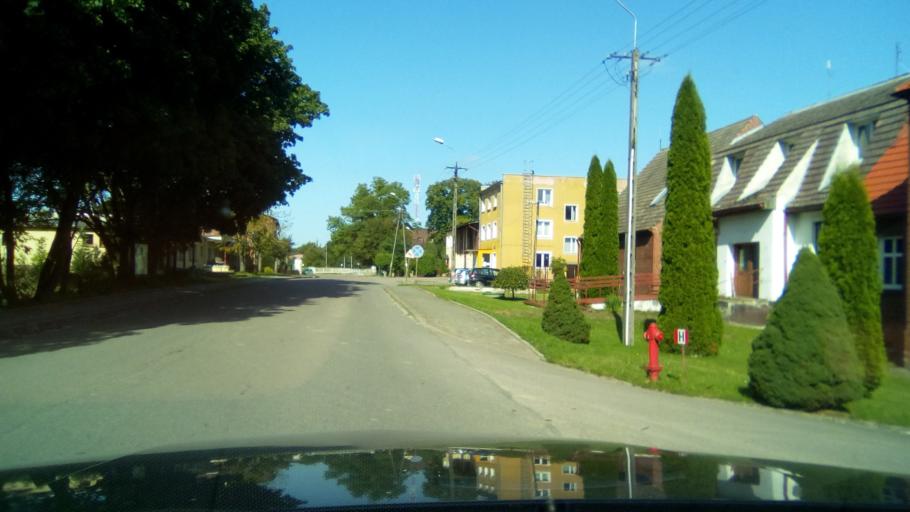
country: PL
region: West Pomeranian Voivodeship
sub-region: Powiat szczecinecki
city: Borne Sulinowo
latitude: 53.6328
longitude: 16.4929
